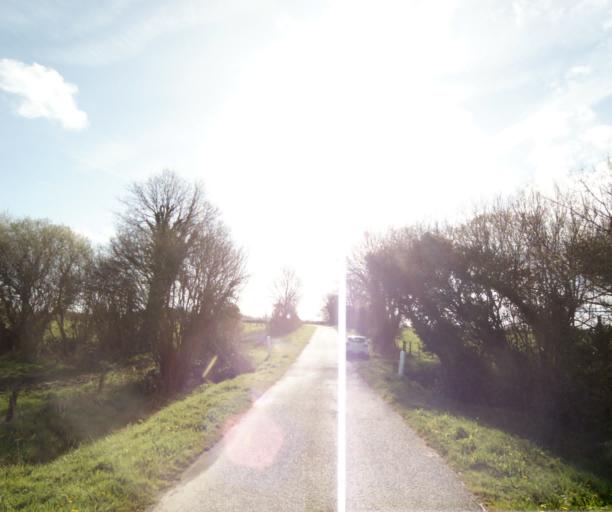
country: FR
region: Pays de la Loire
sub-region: Departement de la Loire-Atlantique
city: Bouvron
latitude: 47.4002
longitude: -1.8343
